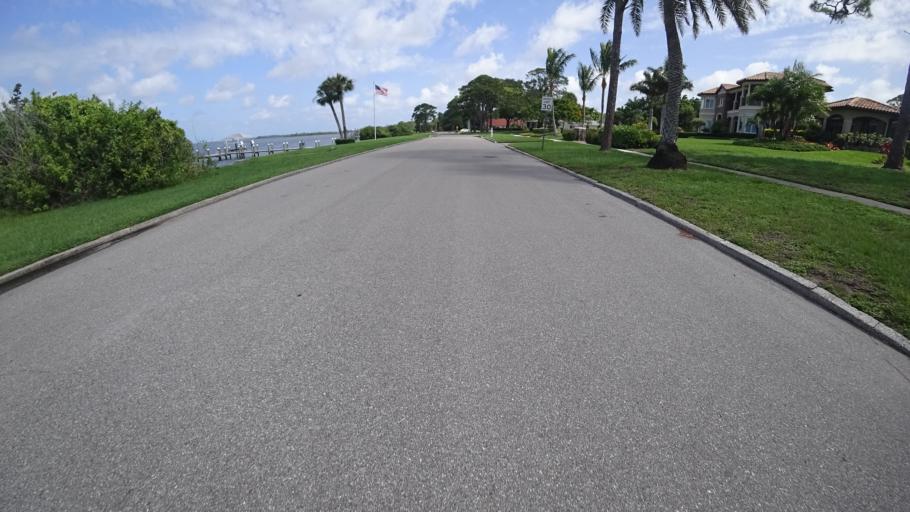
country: US
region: Florida
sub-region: Manatee County
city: Whitfield
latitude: 27.3993
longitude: -82.5698
